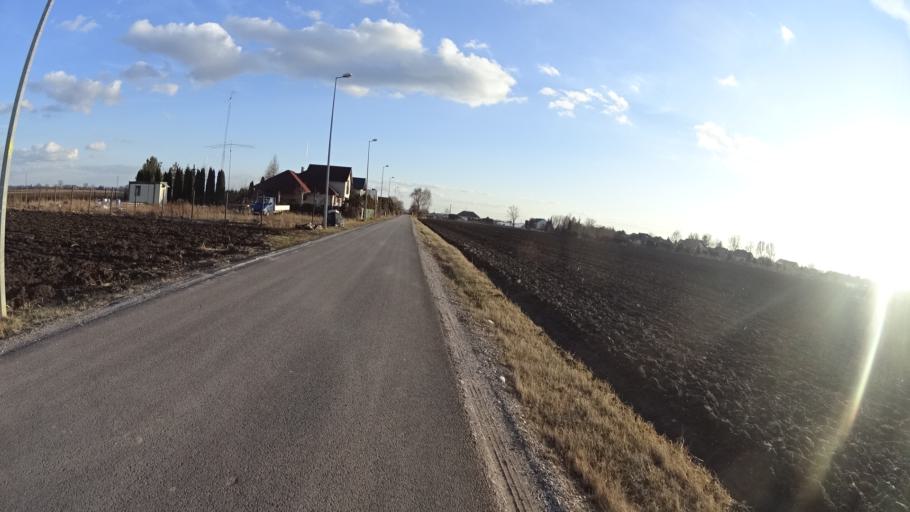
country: PL
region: Masovian Voivodeship
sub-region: Powiat warszawski zachodni
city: Truskaw
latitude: 52.2553
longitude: 20.7566
